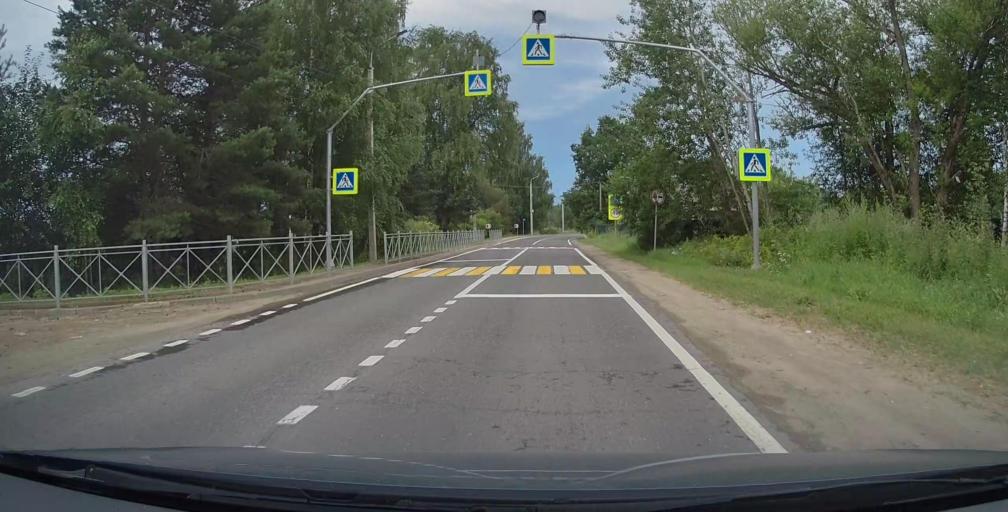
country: RU
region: Jaroslavl
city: Myshkin
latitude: 57.7991
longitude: 38.5076
